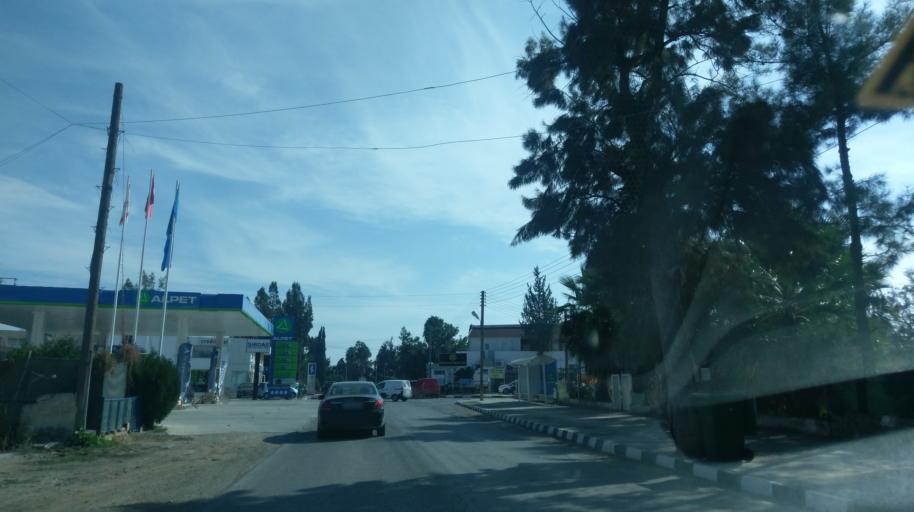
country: CY
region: Larnaka
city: Pergamos
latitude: 35.1104
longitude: 33.6782
